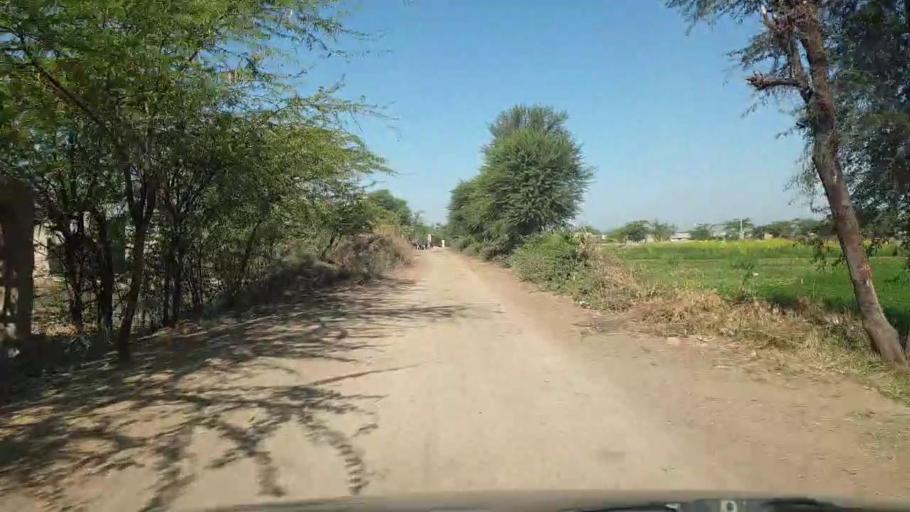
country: PK
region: Sindh
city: Umarkot
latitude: 25.3907
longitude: 69.6962
